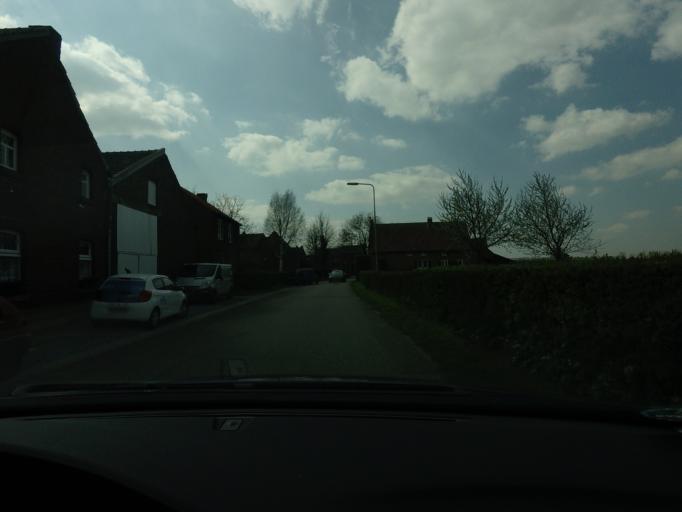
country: NL
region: Limburg
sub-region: Eijsden-Margraten
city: Eijsden
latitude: 50.7645
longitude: 5.7309
